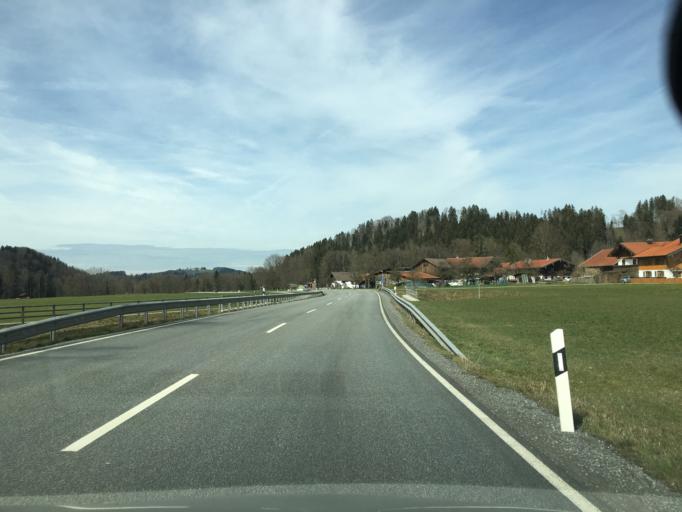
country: DE
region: Bavaria
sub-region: Upper Bavaria
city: Siegsdorf
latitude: 47.8054
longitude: 12.6945
